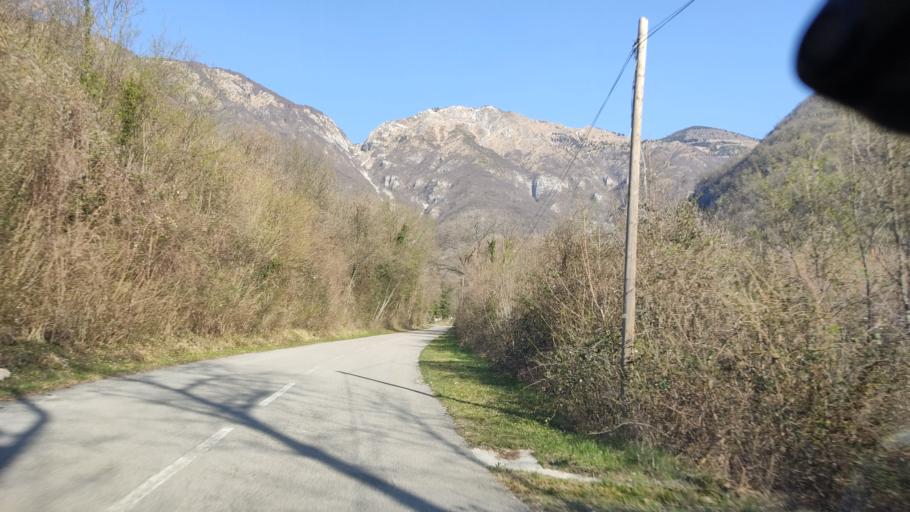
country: IT
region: Friuli Venezia Giulia
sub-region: Provincia di Pordenone
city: Budoia
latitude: 46.0649
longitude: 12.5143
